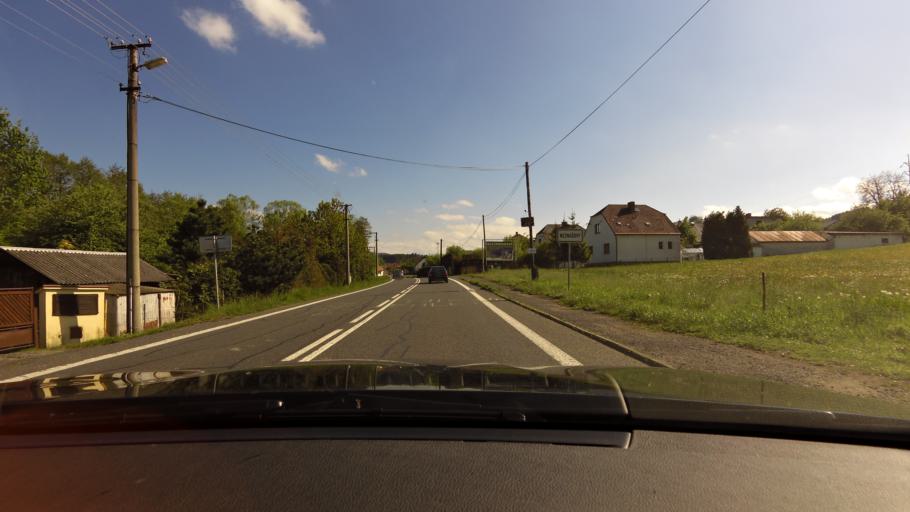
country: CZ
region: Plzensky
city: Strazov
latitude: 49.3298
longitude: 13.3022
